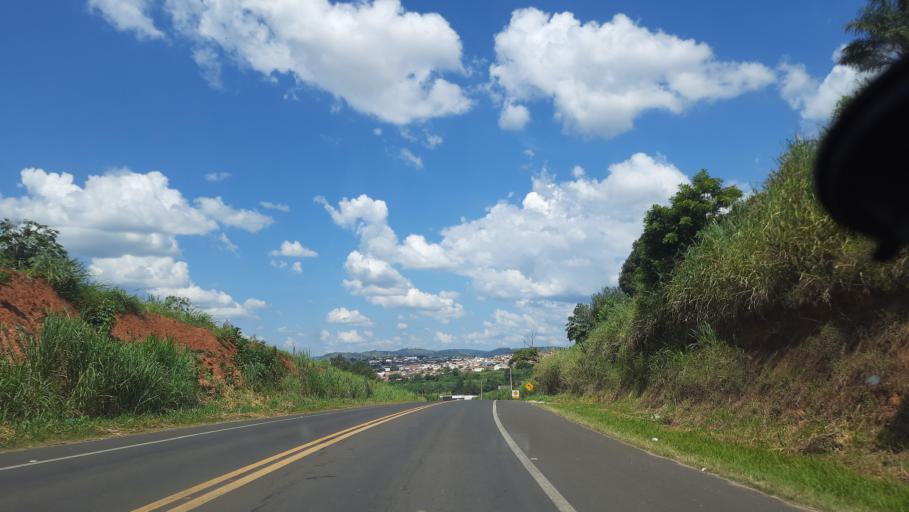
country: BR
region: Sao Paulo
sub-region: Sao Jose Do Rio Pardo
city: Sao Jose do Rio Pardo
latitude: -21.6033
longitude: -46.9196
